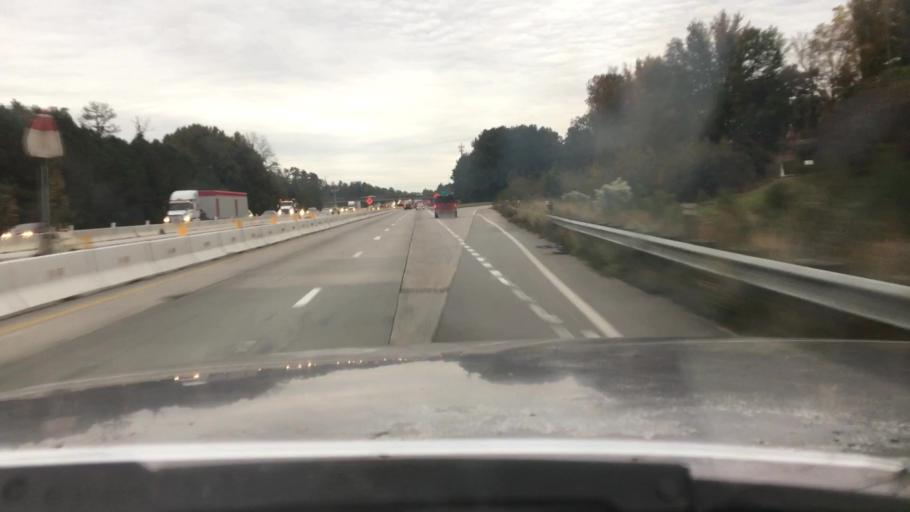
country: US
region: South Carolina
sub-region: Lexington County
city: Lexington
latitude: 33.9826
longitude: -81.1933
